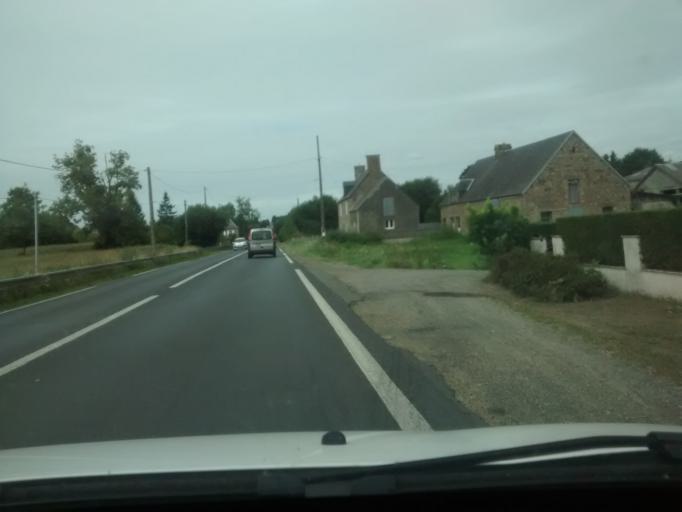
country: FR
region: Lower Normandy
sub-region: Departement de la Manche
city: Marcey-les-Greves
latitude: 48.7099
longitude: -1.3966
